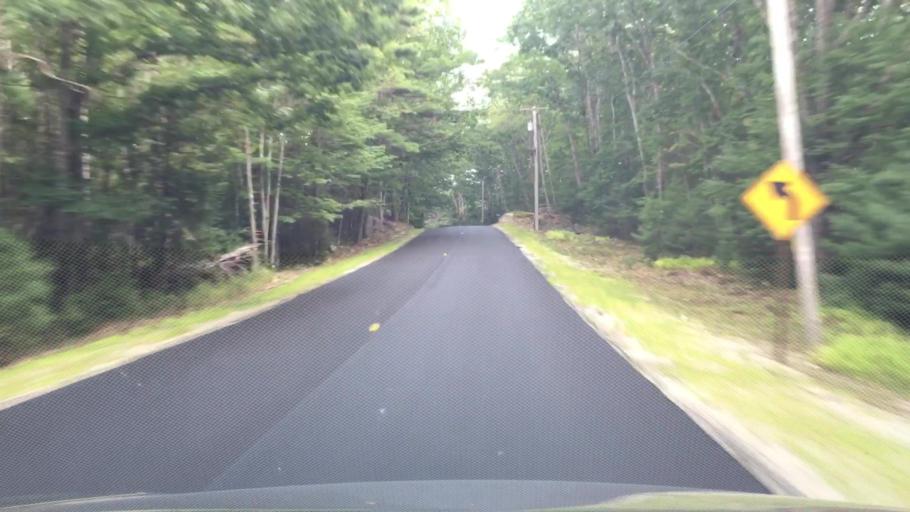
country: US
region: Maine
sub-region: Hancock County
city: Surry
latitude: 44.5207
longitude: -68.6080
